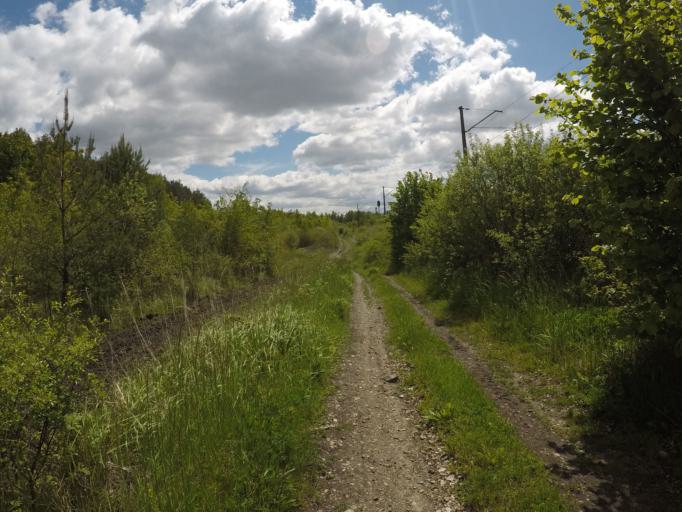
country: PL
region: Swietokrzyskie
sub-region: Powiat kielecki
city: Kostomloty Pierwsze
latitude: 50.9292
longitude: 20.6032
